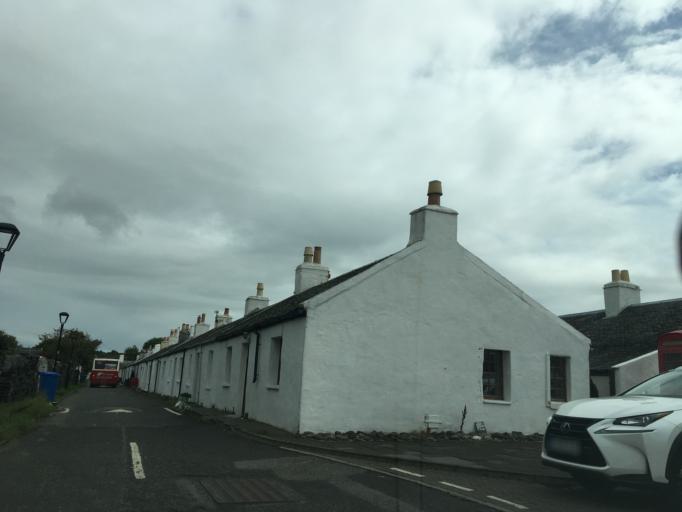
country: GB
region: Scotland
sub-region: Argyll and Bute
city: Isle Of Mull
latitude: 56.2946
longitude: -5.6497
